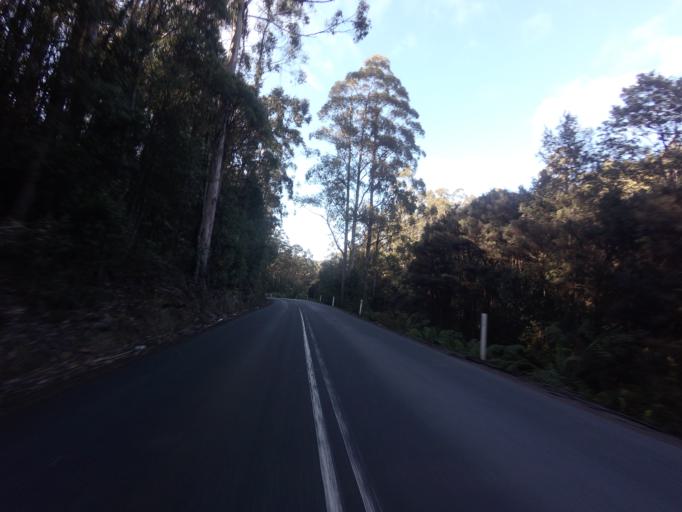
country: AU
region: Tasmania
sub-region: Huon Valley
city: Cygnet
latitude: -43.2605
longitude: 147.0074
